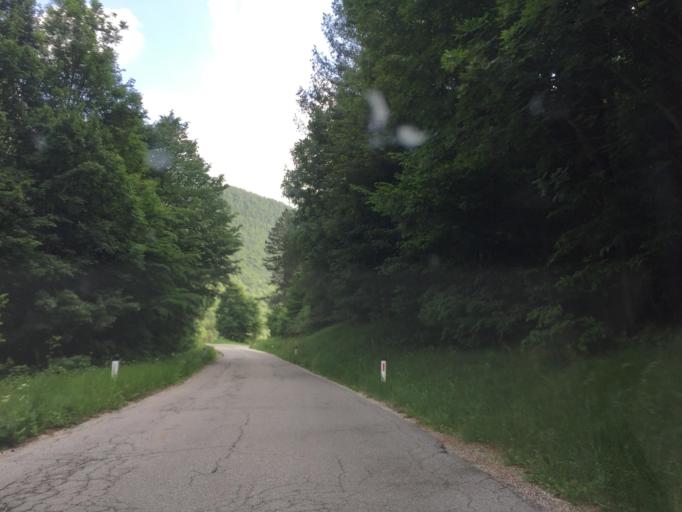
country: SI
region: Nova Gorica
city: Sempas
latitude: 46.0282
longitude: 13.7793
